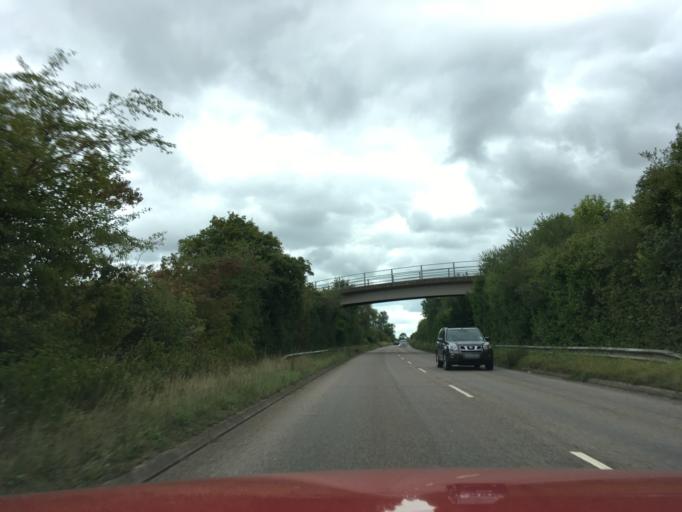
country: GB
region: England
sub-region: Devon
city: Exminster
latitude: 50.6826
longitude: -3.4903
